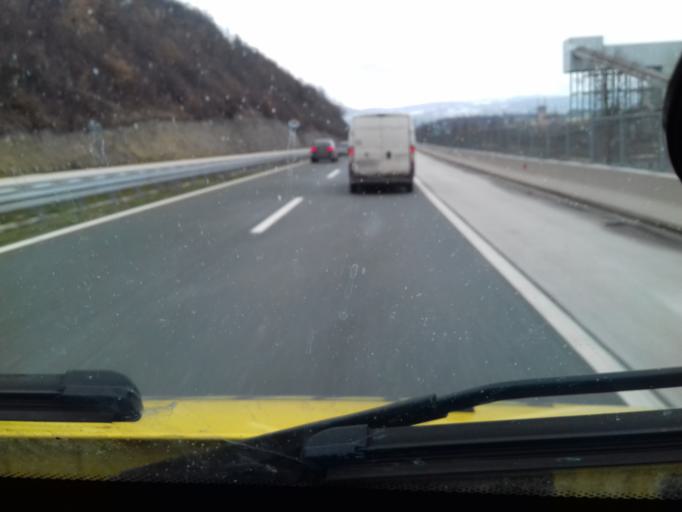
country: BA
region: Federation of Bosnia and Herzegovina
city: Dobrinje
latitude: 44.0875
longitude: 18.1120
